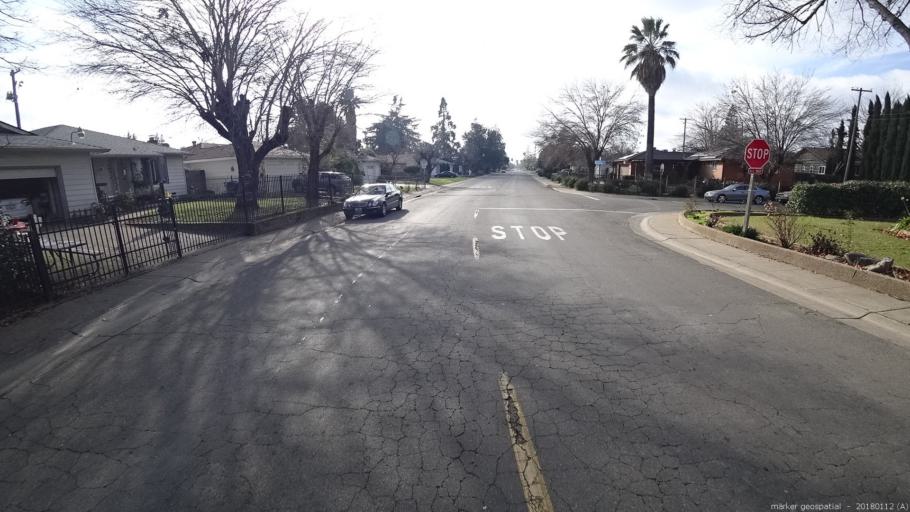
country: US
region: California
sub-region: Sacramento County
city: Rancho Cordova
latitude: 38.5923
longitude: -121.3016
